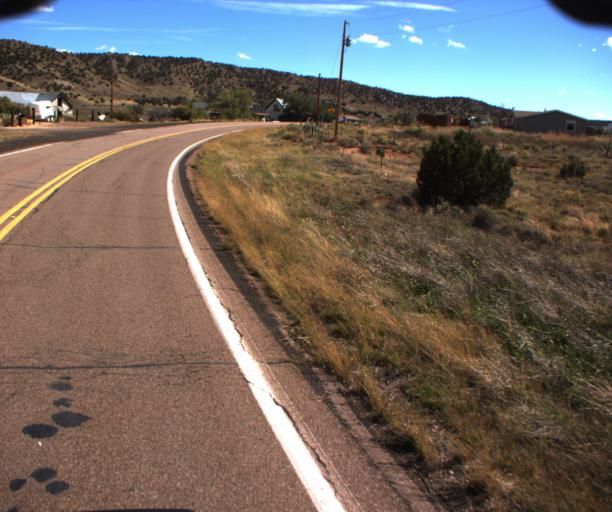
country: US
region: Arizona
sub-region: Apache County
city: Saint Johns
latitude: 34.4778
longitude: -109.6039
